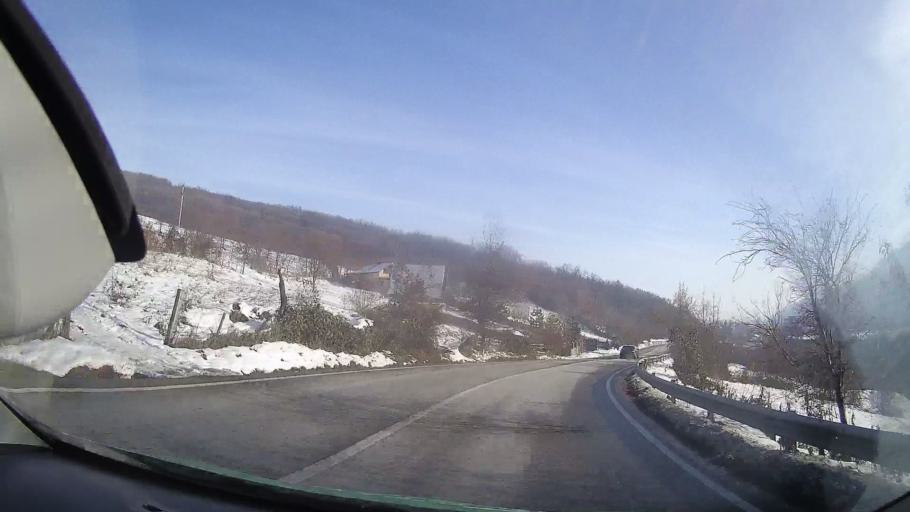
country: RO
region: Neamt
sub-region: Comuna Garcina
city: Garcina
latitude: 46.9773
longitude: 26.3589
